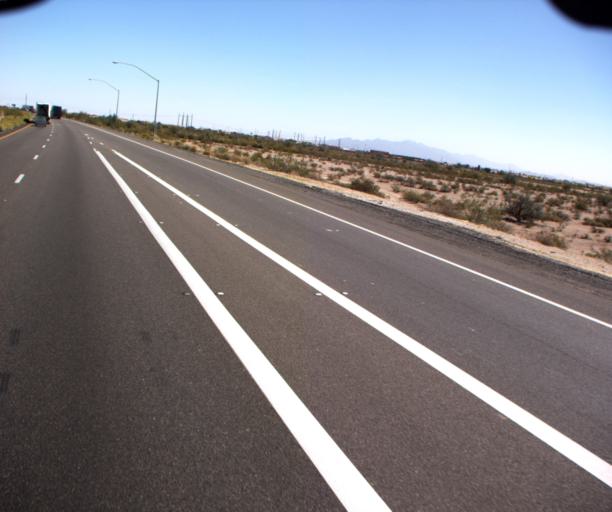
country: US
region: Arizona
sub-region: Maricopa County
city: Buckeye
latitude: 33.4269
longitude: -112.6171
